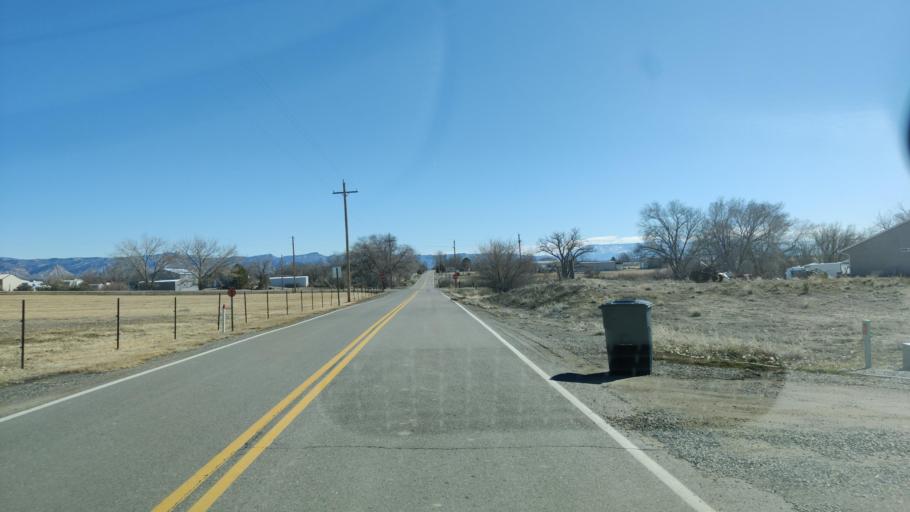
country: US
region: Colorado
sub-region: Mesa County
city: Fruita
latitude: 39.1788
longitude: -108.7120
